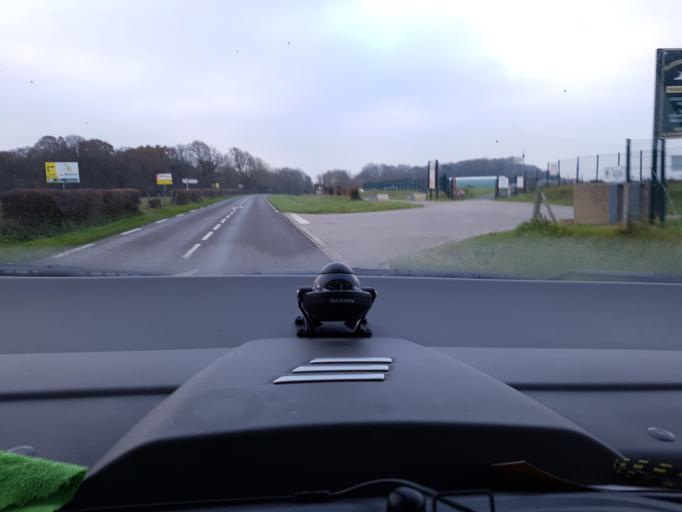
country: FR
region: Haute-Normandie
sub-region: Departement de la Seine-Maritime
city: Eu
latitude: 50.0702
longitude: 1.4315
